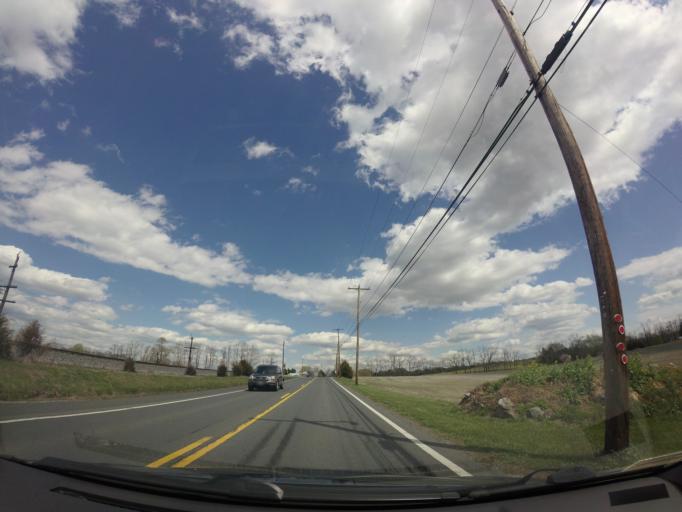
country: US
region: West Virginia
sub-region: Jefferson County
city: Shepherdstown
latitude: 39.4498
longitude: -77.7707
